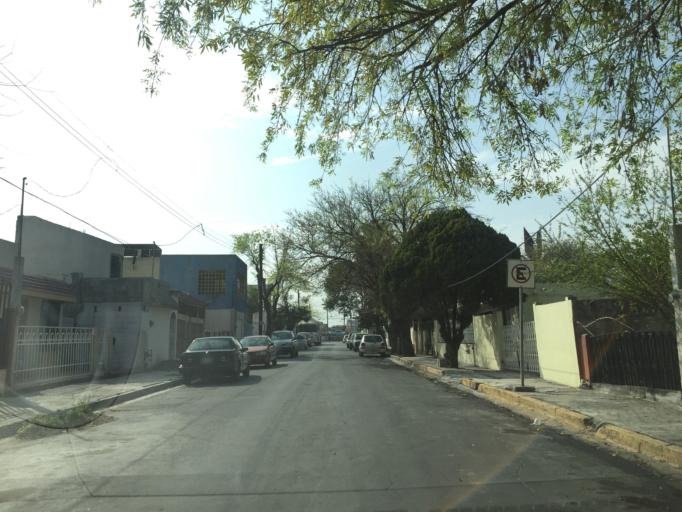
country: MX
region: Nuevo Leon
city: Guadalupe
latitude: 25.7067
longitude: -100.2220
